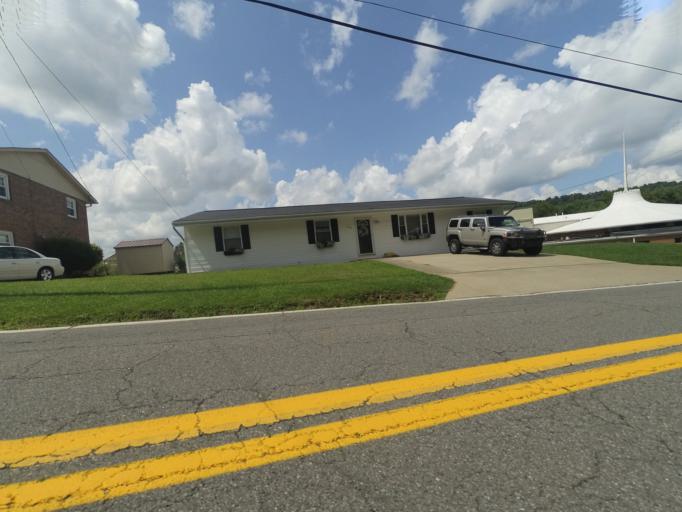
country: US
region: West Virginia
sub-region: Cabell County
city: Pea Ridge
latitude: 38.4112
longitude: -82.3632
